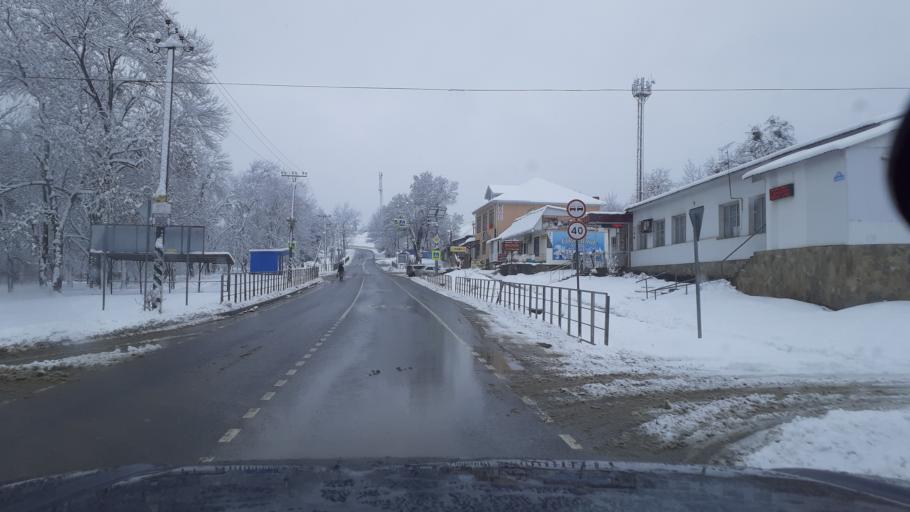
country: RU
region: Adygeya
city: Kamennomostskiy
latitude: 44.2326
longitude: 40.2017
